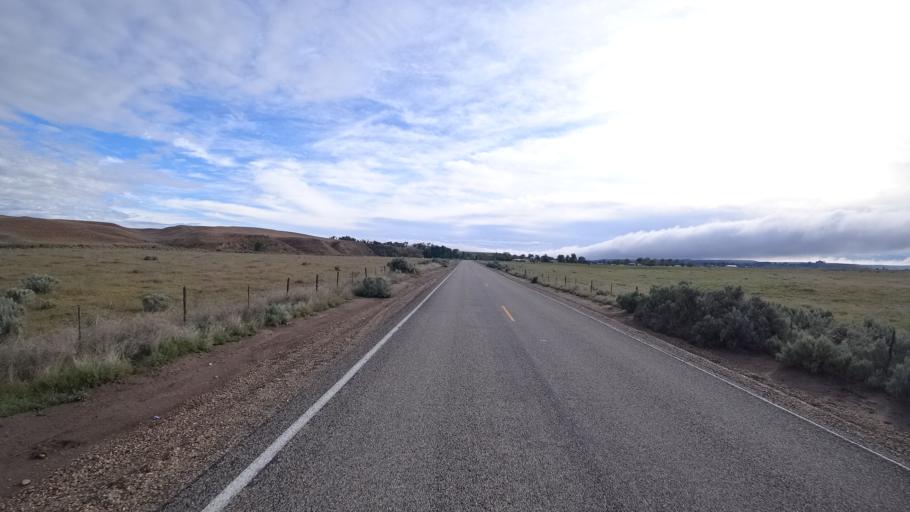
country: US
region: Idaho
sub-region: Ada County
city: Star
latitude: 43.7690
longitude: -116.4957
